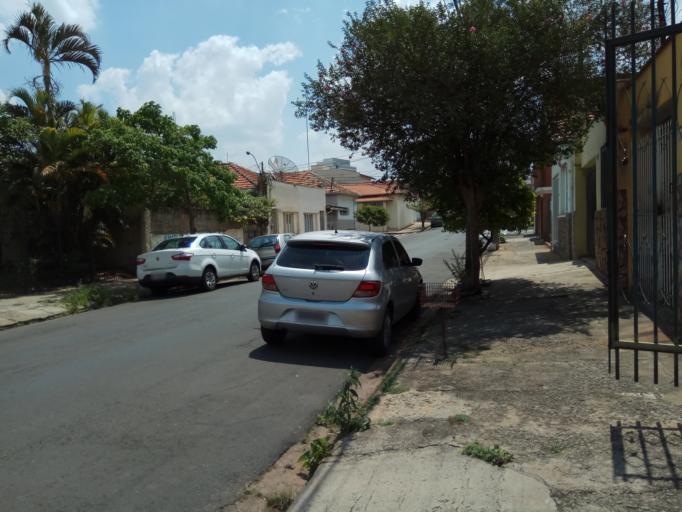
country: BR
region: Sao Paulo
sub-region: Piracicaba
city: Piracicaba
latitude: -22.7156
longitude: -47.6420
